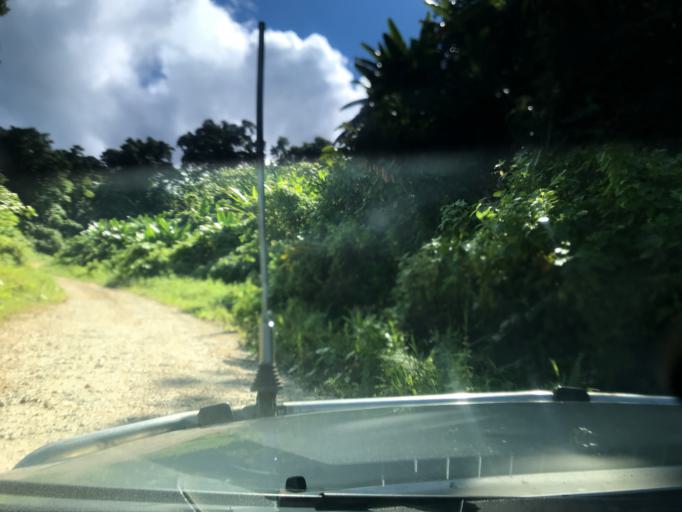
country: SB
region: Malaita
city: Auki
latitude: -8.6537
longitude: 160.7610
